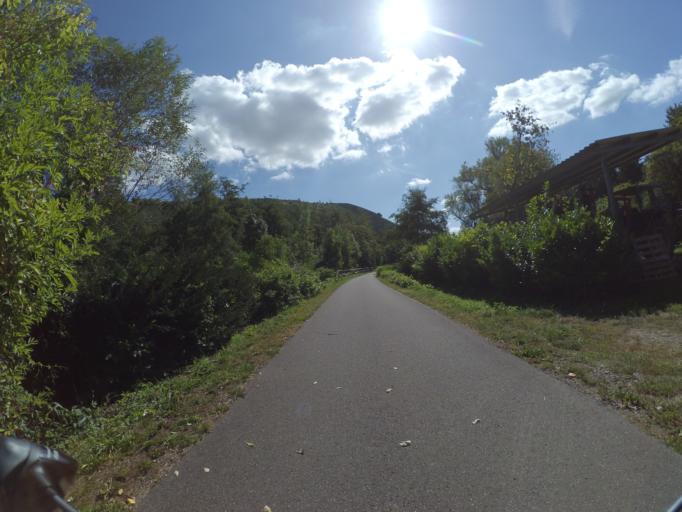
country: DE
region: Rheinland-Pfalz
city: Mertesdorf
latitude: 49.7689
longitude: 6.7255
